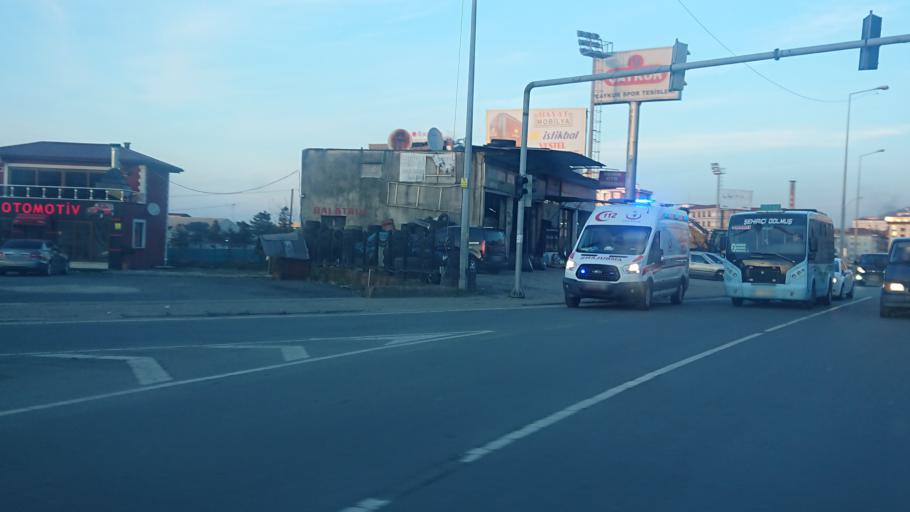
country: TR
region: Rize
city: Gundogdu
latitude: 41.0430
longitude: 40.5797
